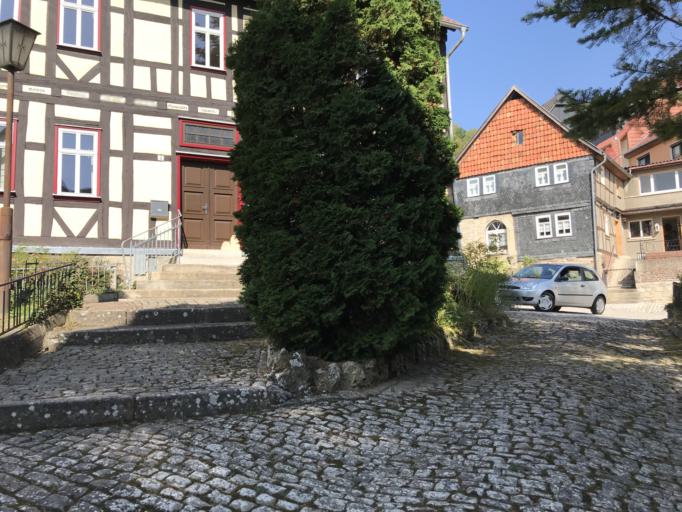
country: DE
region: Thuringia
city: Treffurt
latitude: 51.1380
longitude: 10.2368
